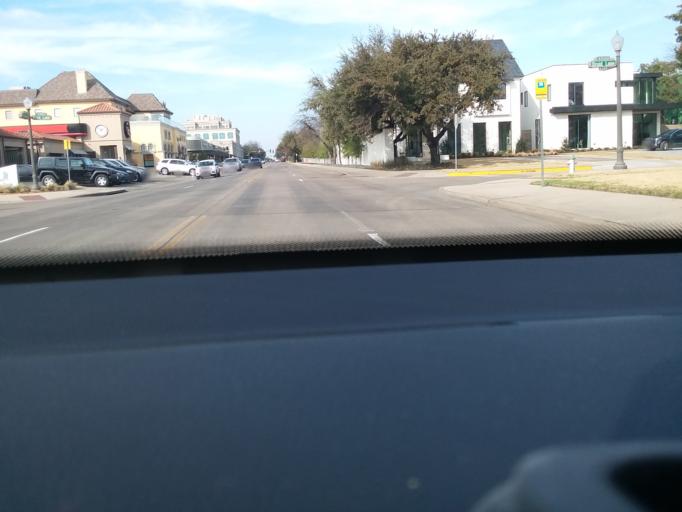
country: US
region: Texas
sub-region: Dallas County
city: University Park
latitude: 32.8481
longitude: -96.8043
